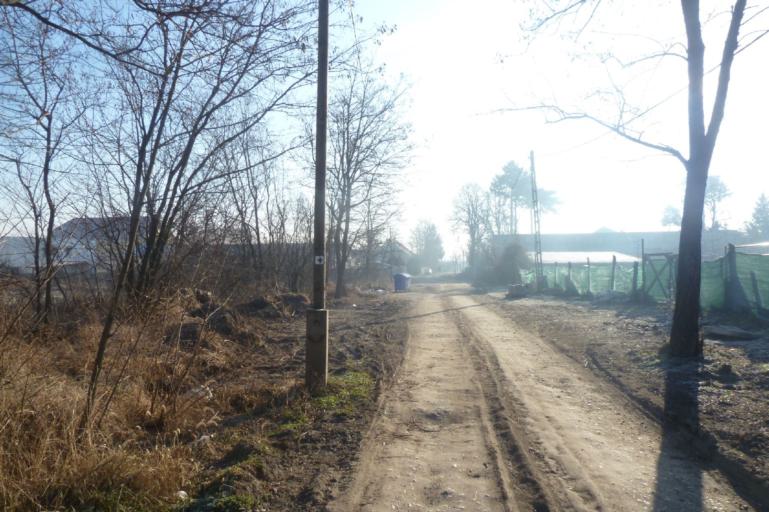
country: HU
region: Pest
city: Isaszeg
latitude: 47.5266
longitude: 19.4344
